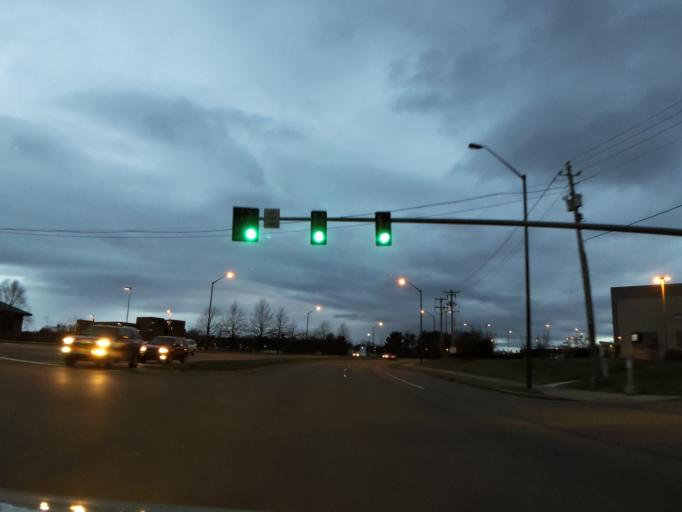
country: US
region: Tennessee
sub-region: Washington County
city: Johnson City
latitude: 36.3054
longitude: -82.3856
